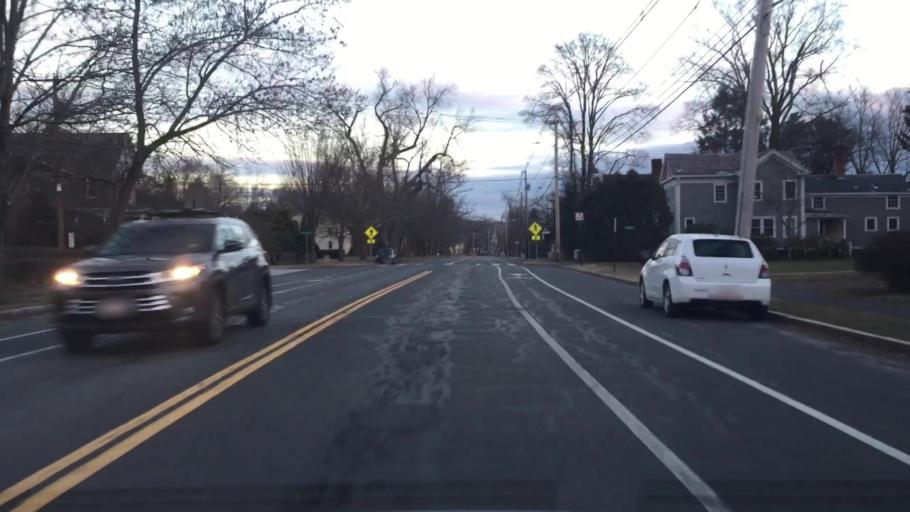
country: US
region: Massachusetts
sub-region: Hampshire County
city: Northampton
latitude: 42.3227
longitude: -72.6449
